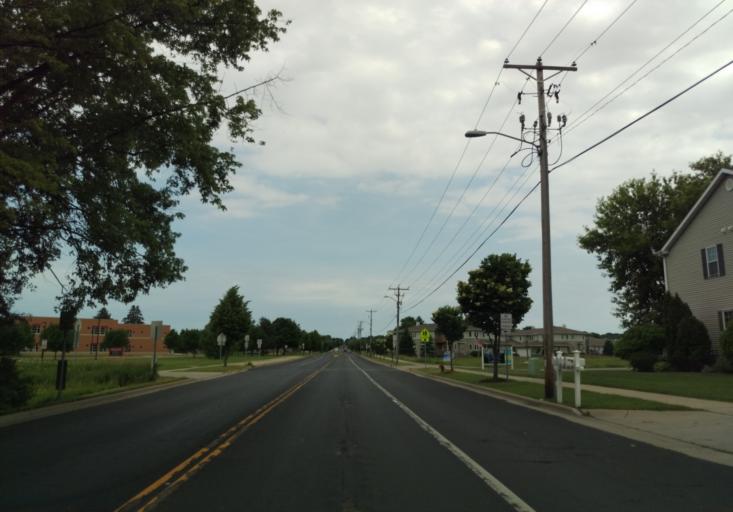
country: US
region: Wisconsin
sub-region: Dane County
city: Verona
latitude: 43.0081
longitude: -89.4990
